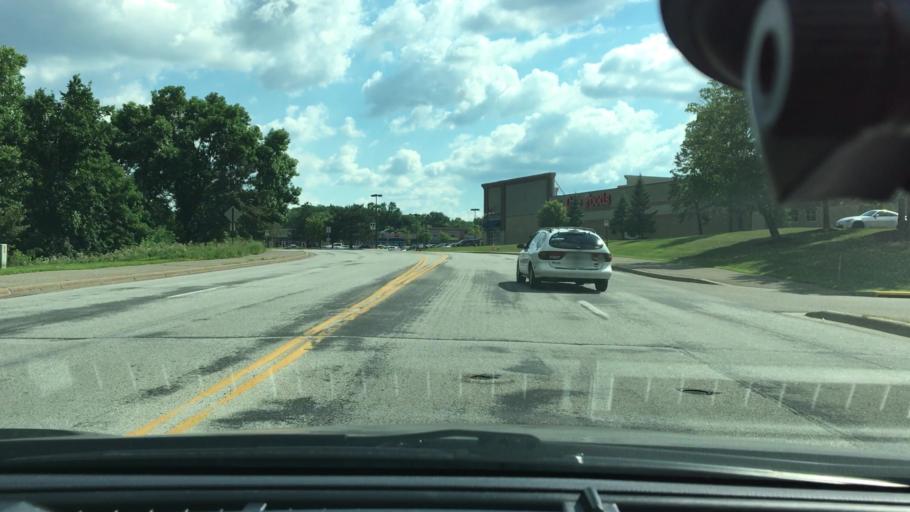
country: US
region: Minnesota
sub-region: Hennepin County
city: New Hope
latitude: 45.0361
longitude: -93.4082
